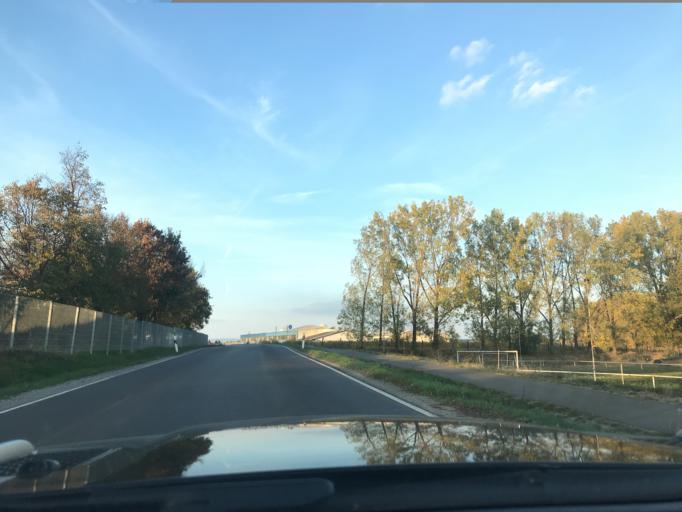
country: DE
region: Thuringia
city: Niederdorla
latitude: 51.1525
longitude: 10.4406
